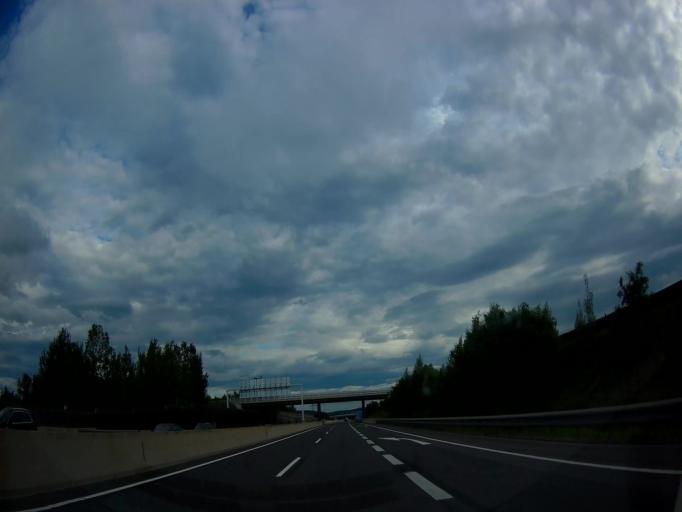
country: AT
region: Lower Austria
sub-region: Politischer Bezirk Sankt Polten
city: Traismauer
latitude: 48.3660
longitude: 15.7183
